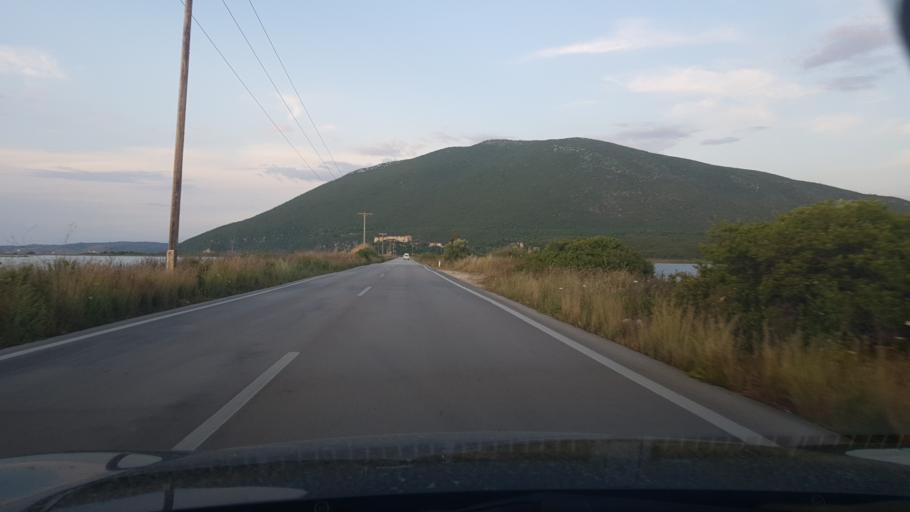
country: GR
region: Ionian Islands
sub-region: Lefkada
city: Lefkada
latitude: 38.8446
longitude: 20.7279
